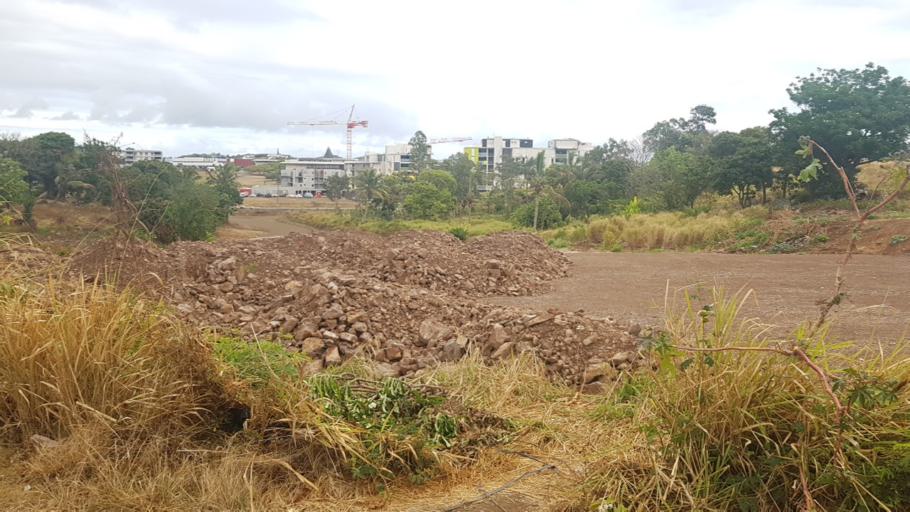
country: NC
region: South Province
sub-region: Noumea
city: Noumea
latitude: -22.2161
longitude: 166.4767
